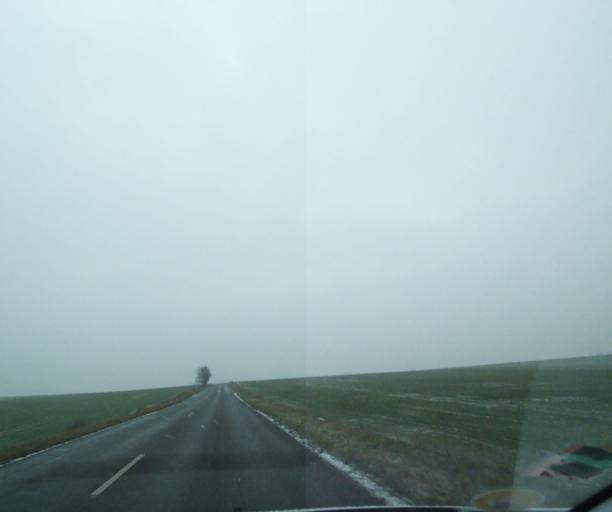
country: FR
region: Champagne-Ardenne
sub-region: Departement de la Haute-Marne
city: Wassy
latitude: 48.4842
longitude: 4.9889
